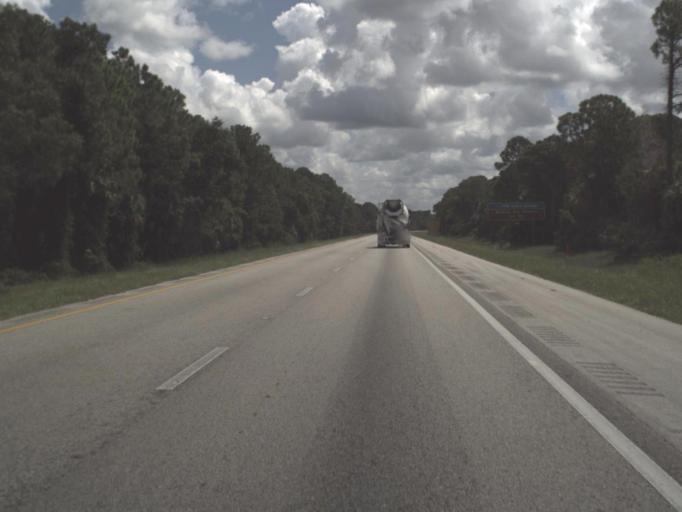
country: US
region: Florida
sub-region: Collier County
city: Golden Gate
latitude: 26.1636
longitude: -81.7097
